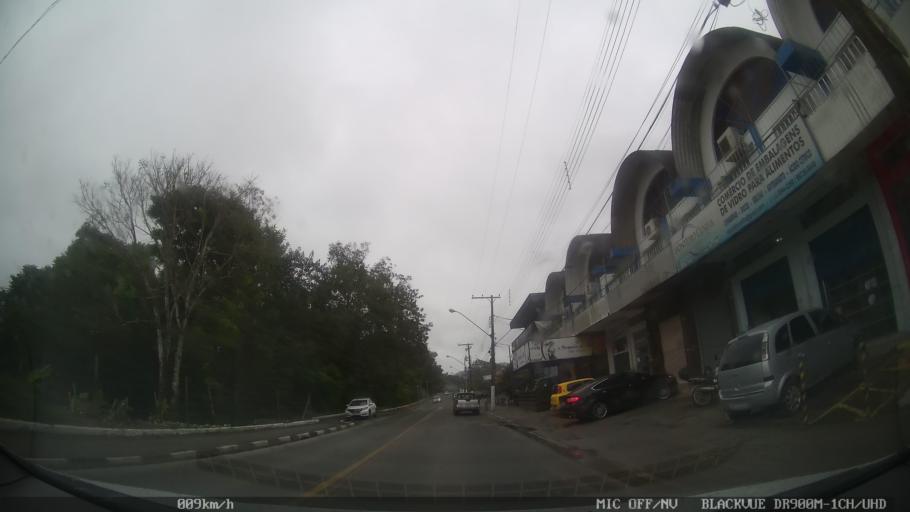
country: BR
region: Sao Paulo
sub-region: Juquia
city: Juquia
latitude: -24.3257
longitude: -47.6326
